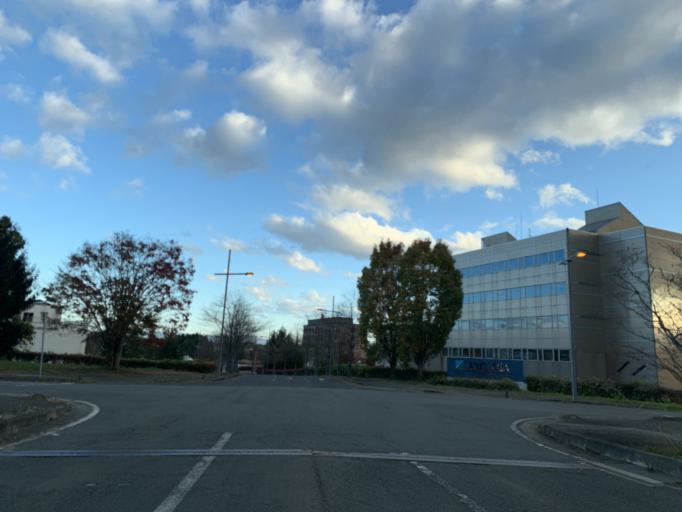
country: JP
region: Iwate
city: Kitakami
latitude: 39.2583
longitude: 141.1055
